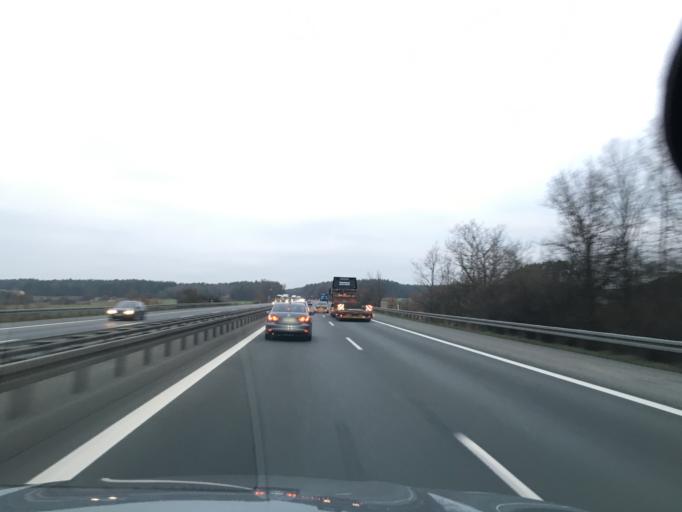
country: DE
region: Bavaria
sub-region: Regierungsbezirk Mittelfranken
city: Hessdorf
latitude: 49.6525
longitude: 10.8994
